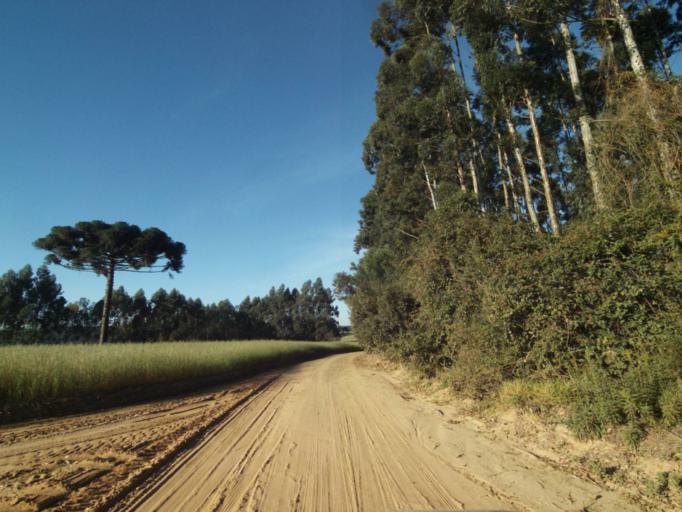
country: BR
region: Parana
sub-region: Tibagi
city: Tibagi
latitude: -24.5366
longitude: -50.6079
